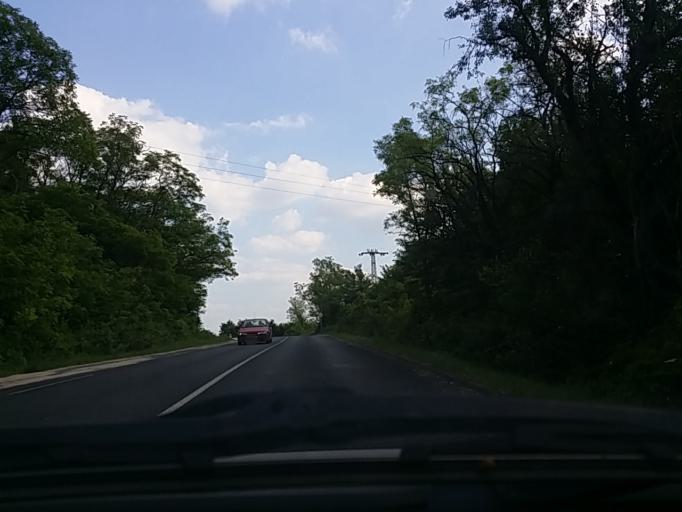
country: HU
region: Pest
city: Csobanka
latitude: 47.6675
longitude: 18.9572
